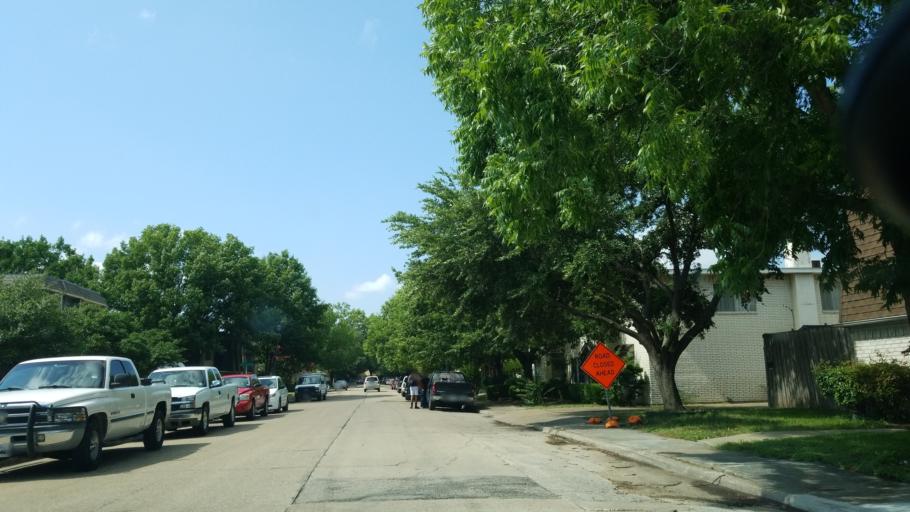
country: US
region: Texas
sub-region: Dallas County
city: Farmers Branch
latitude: 32.8808
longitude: -96.8582
